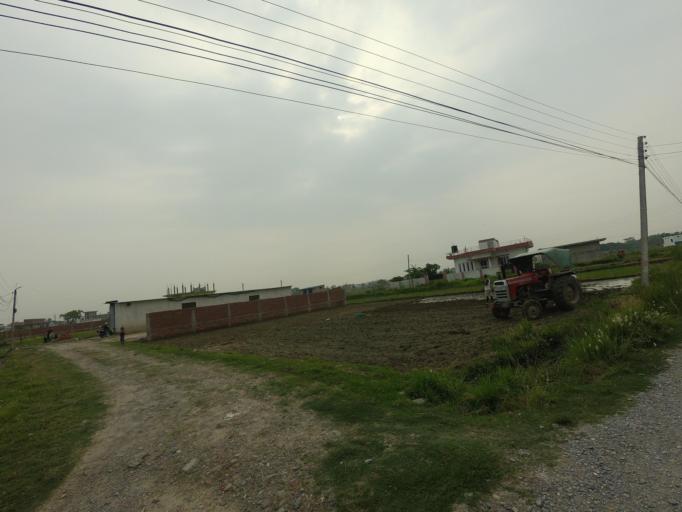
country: NP
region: Western Region
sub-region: Lumbini Zone
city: Bhairahawa
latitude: 27.4894
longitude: 83.4535
